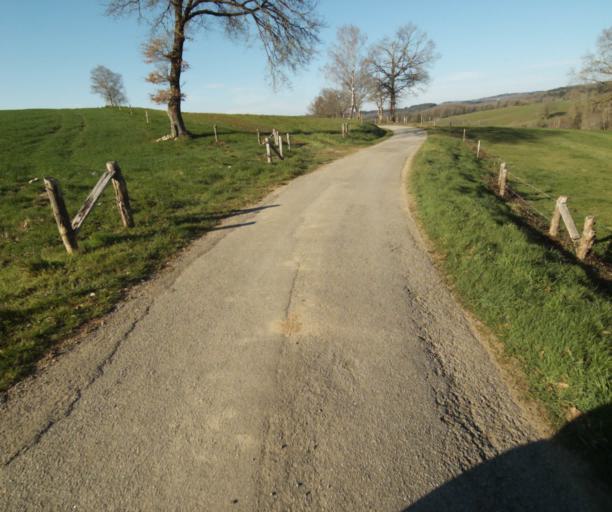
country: FR
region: Limousin
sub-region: Departement de la Correze
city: Chamboulive
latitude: 45.4833
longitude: 1.7306
